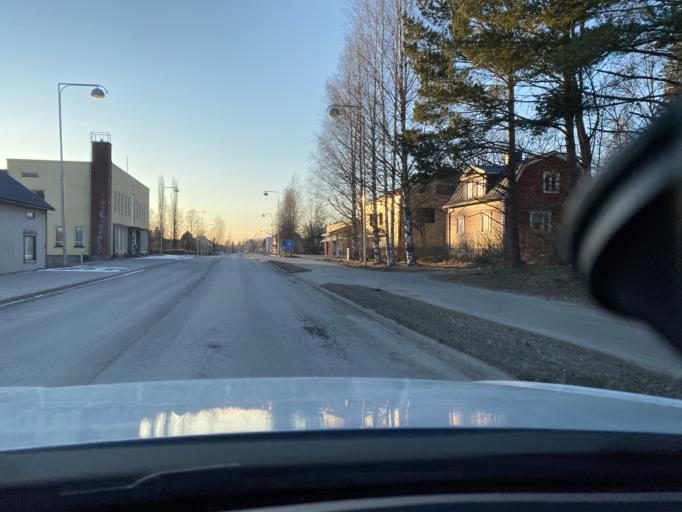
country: FI
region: Pirkanmaa
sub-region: Lounais-Pirkanmaa
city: Punkalaidun
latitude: 61.1108
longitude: 23.1119
